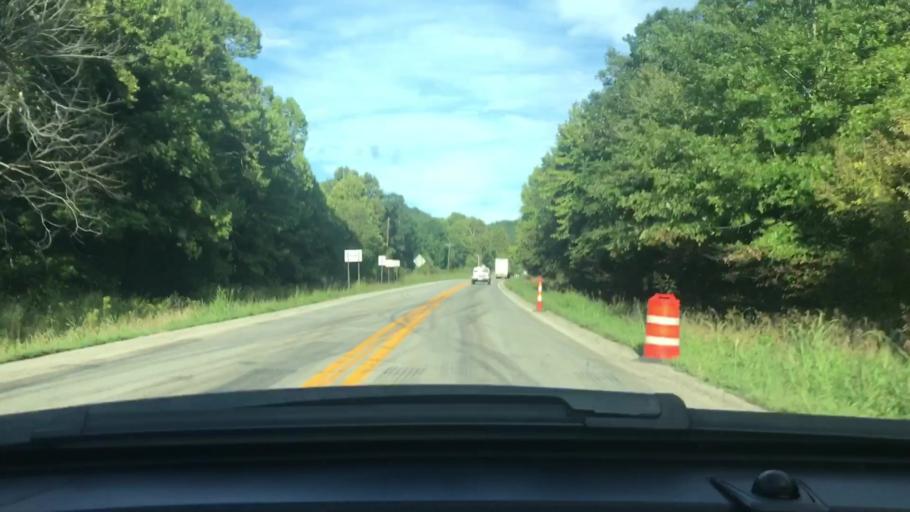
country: US
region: Arkansas
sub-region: Sharp County
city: Cherokee Village
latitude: 36.3033
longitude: -91.4254
